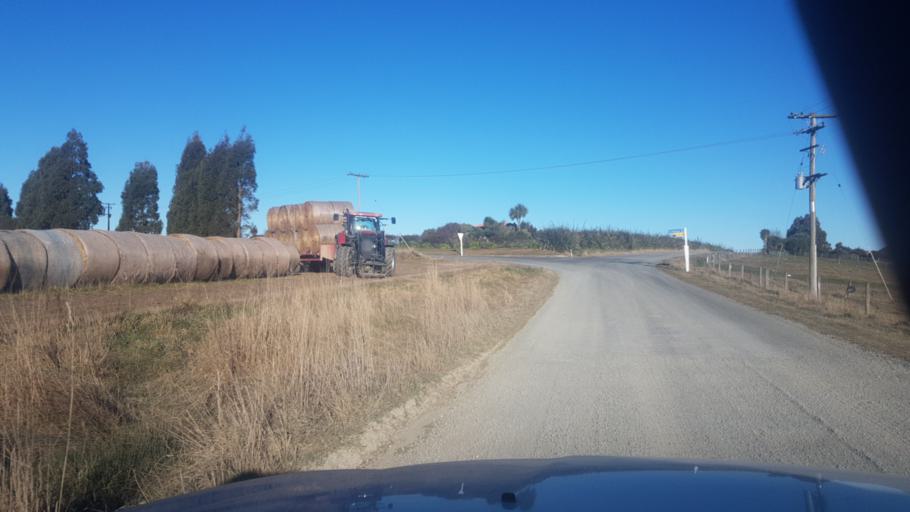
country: NZ
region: Canterbury
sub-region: Timaru District
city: Pleasant Point
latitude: -44.3592
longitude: 171.0697
